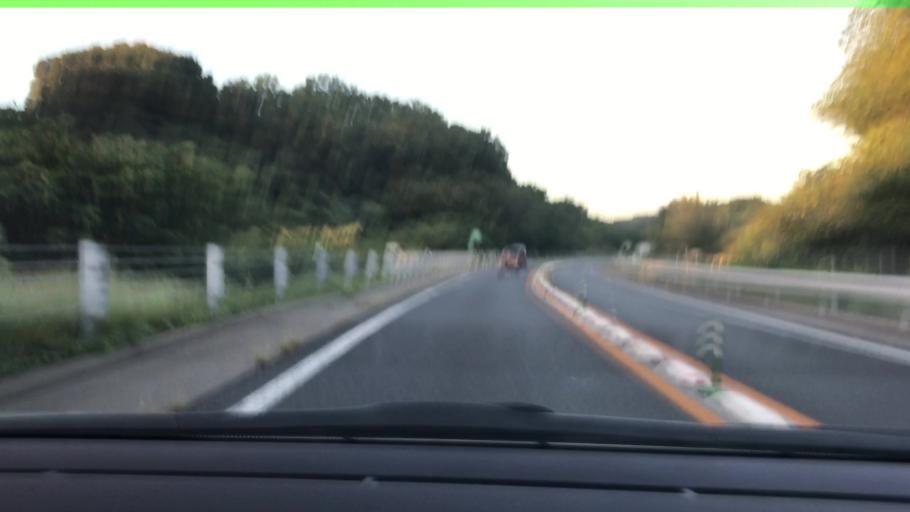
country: JP
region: Hiroshima
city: Innoshima
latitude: 34.3263
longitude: 133.1509
